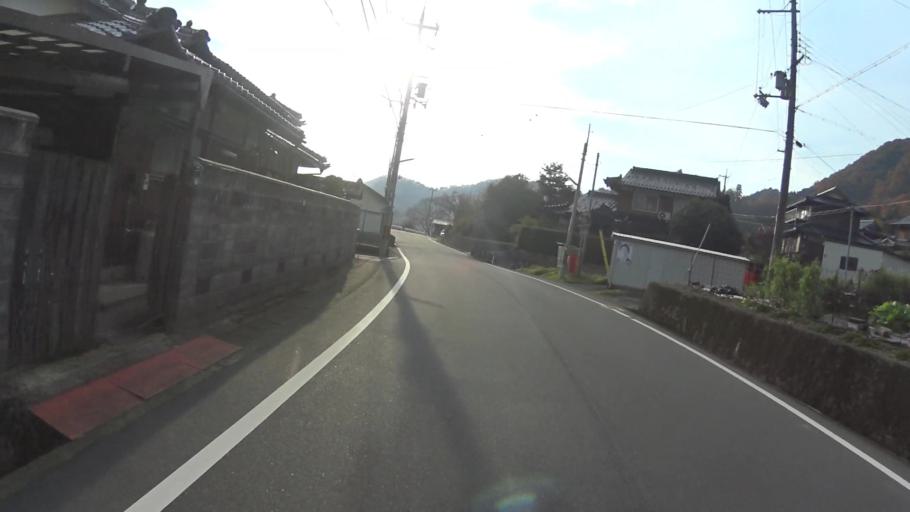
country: JP
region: Kyoto
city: Maizuru
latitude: 35.5254
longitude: 135.4118
